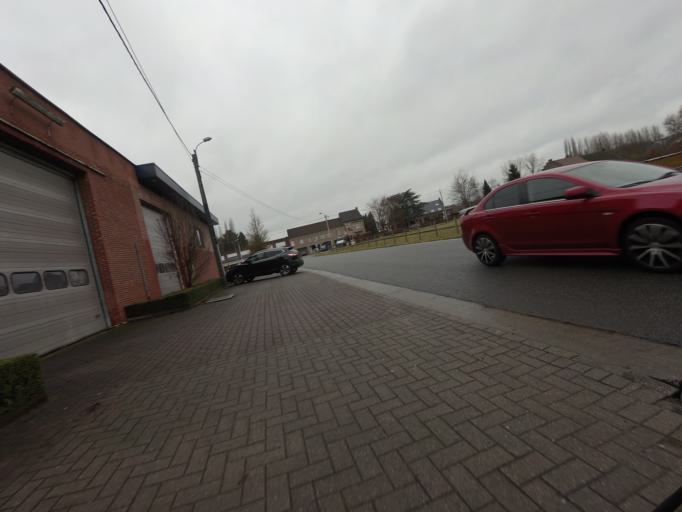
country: BE
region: Flanders
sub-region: Provincie Antwerpen
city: Sint-Katelijne-Waver
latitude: 51.0451
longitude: 4.5245
